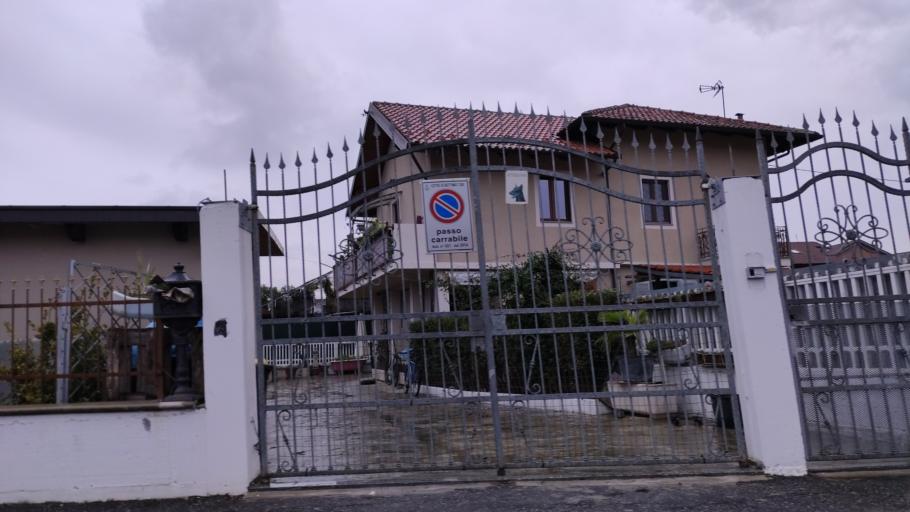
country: IT
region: Piedmont
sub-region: Provincia di Torino
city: Settimo Torinese
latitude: 45.1470
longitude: 7.7698
